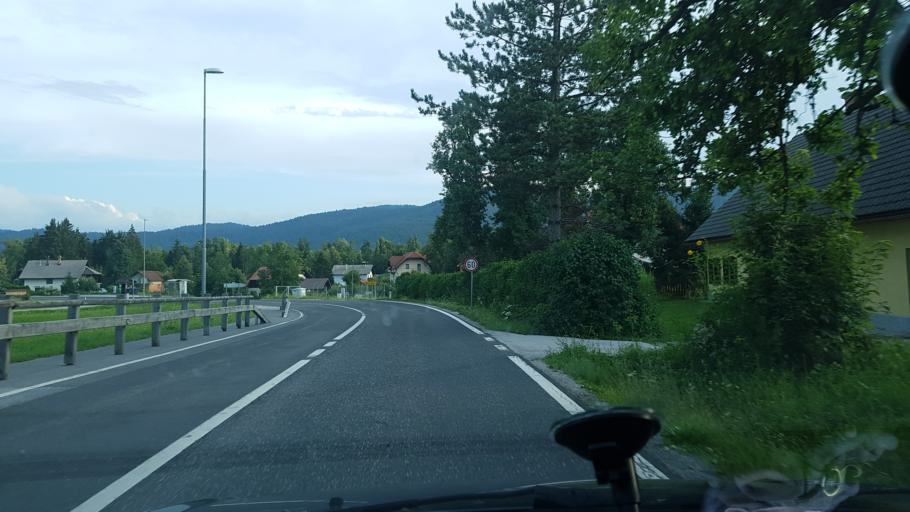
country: SI
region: Logatec
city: Logatec
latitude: 45.9216
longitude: 14.1413
